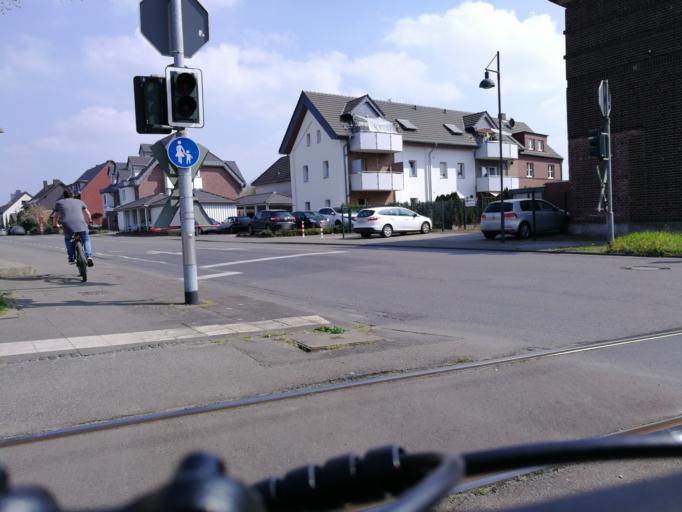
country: DE
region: North Rhine-Westphalia
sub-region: Regierungsbezirk Dusseldorf
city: Dormagen
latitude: 51.1359
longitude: 6.8019
